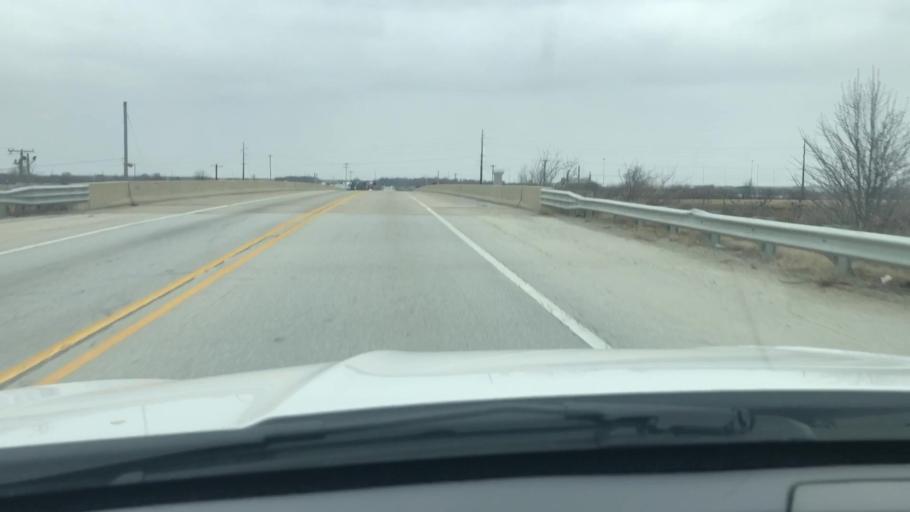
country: US
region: Indiana
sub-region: Tippecanoe County
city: Dayton
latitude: 40.3736
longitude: -86.8141
